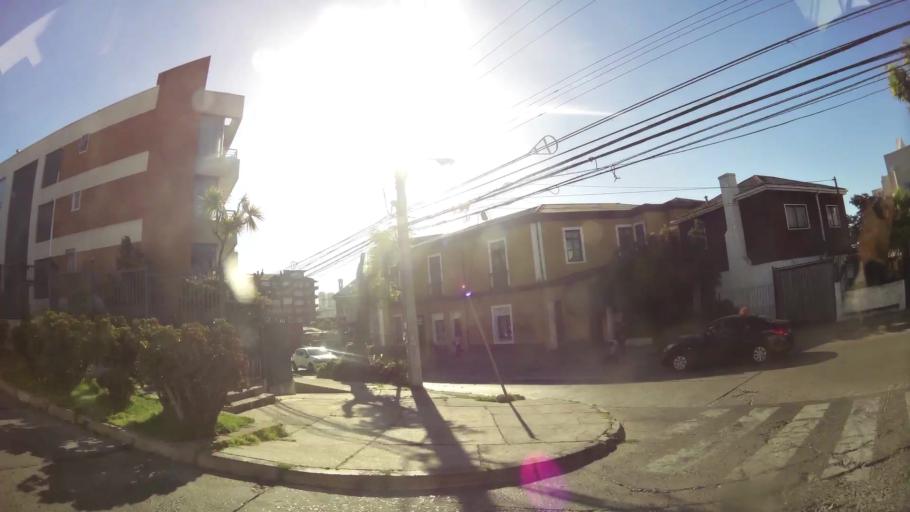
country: CL
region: Valparaiso
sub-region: Provincia de Valparaiso
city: Vina del Mar
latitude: -33.0263
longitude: -71.5686
